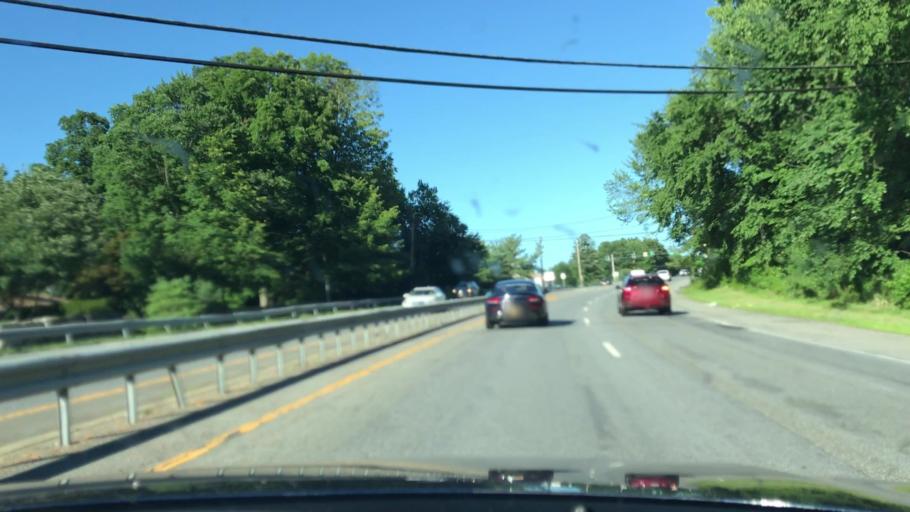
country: US
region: New York
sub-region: Westchester County
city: Jefferson Valley-Yorktown
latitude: 41.3368
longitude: -73.7884
